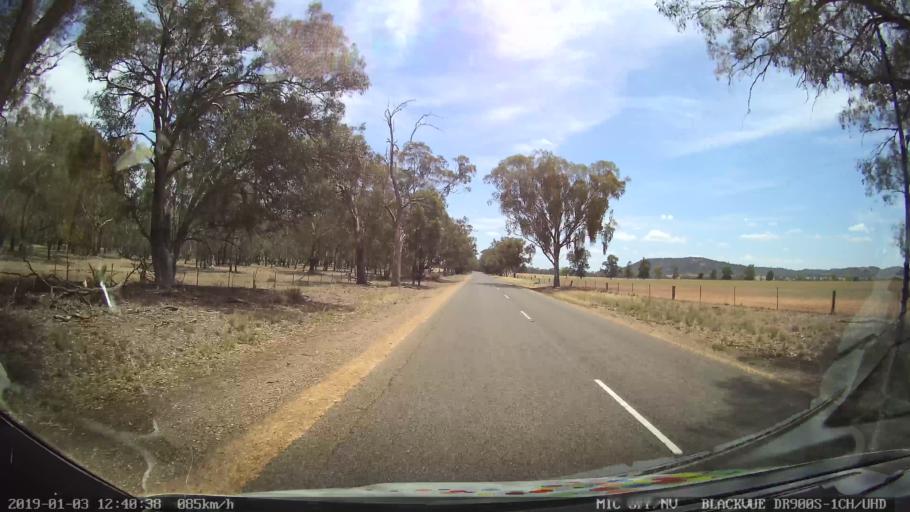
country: AU
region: New South Wales
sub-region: Weddin
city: Grenfell
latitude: -33.8100
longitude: 148.2132
